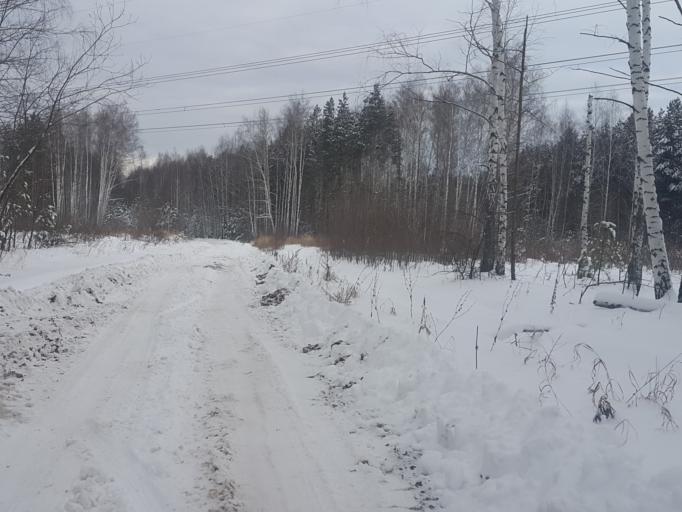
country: RU
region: Tambov
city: Platonovka
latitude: 52.8894
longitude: 41.8523
